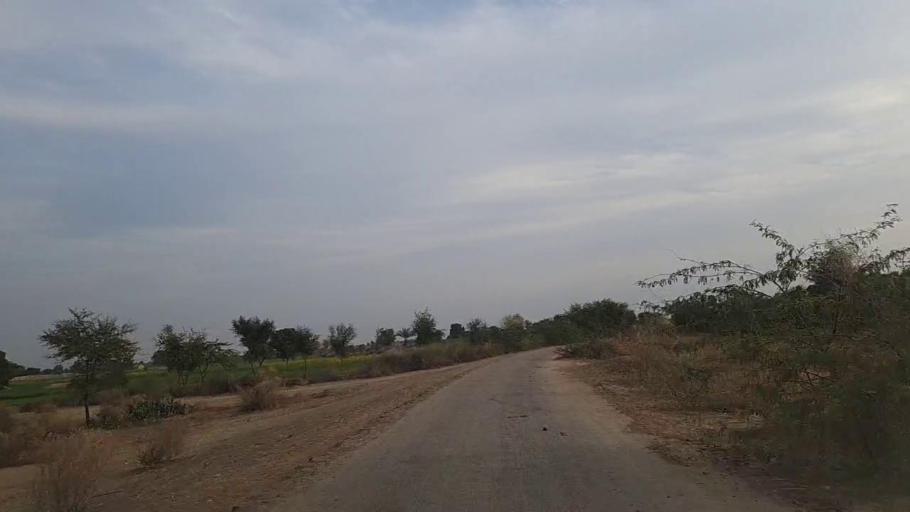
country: PK
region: Sindh
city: Jam Sahib
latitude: 26.4780
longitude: 68.5641
